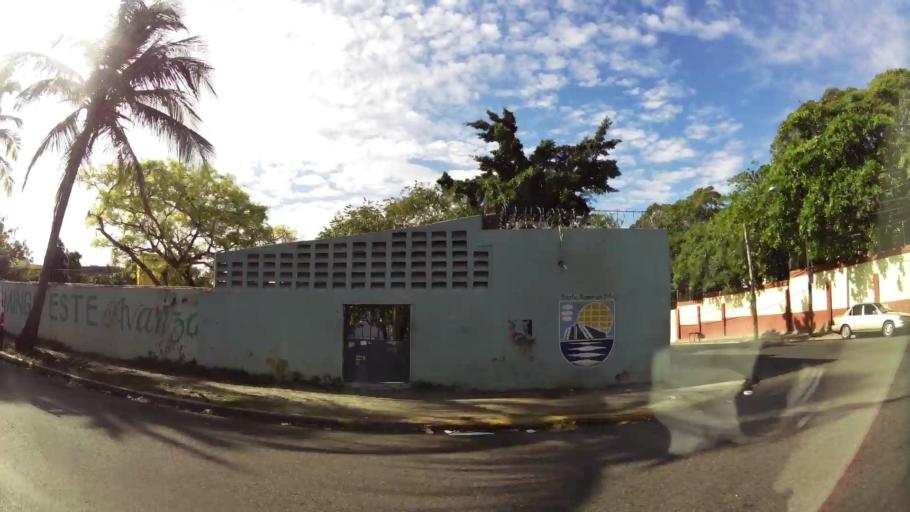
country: DO
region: Santo Domingo
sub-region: Santo Domingo
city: Santo Domingo Este
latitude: 18.4870
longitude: -69.8645
